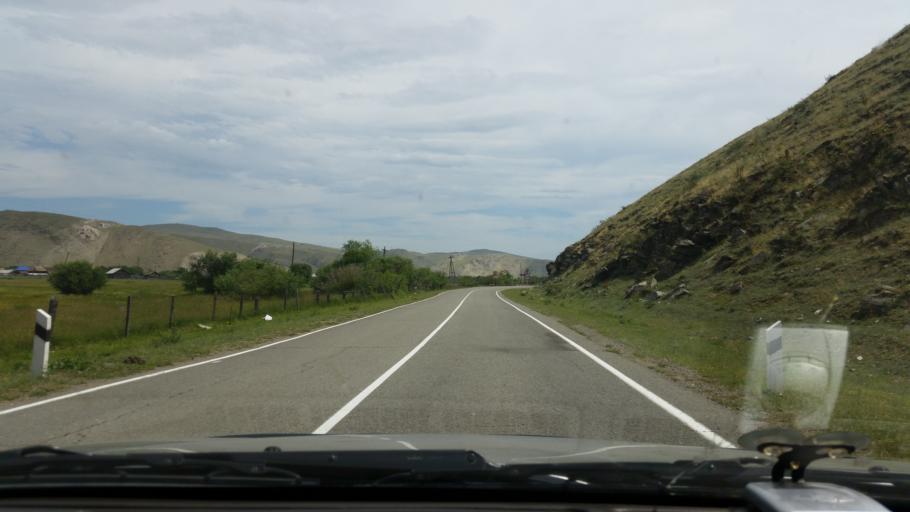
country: RU
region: Irkutsk
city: Yelantsy
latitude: 52.8066
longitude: 106.4622
